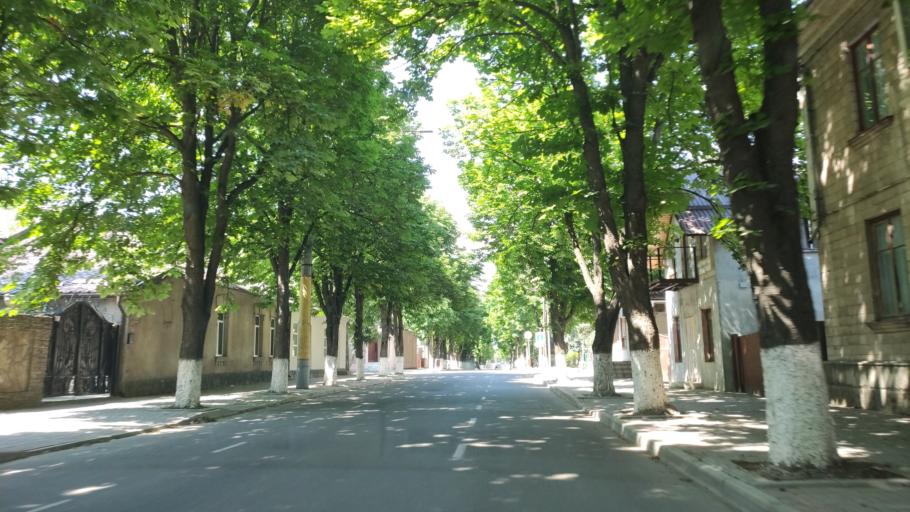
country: MD
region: Raionul Soroca
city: Soroca
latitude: 48.1535
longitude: 28.3021
